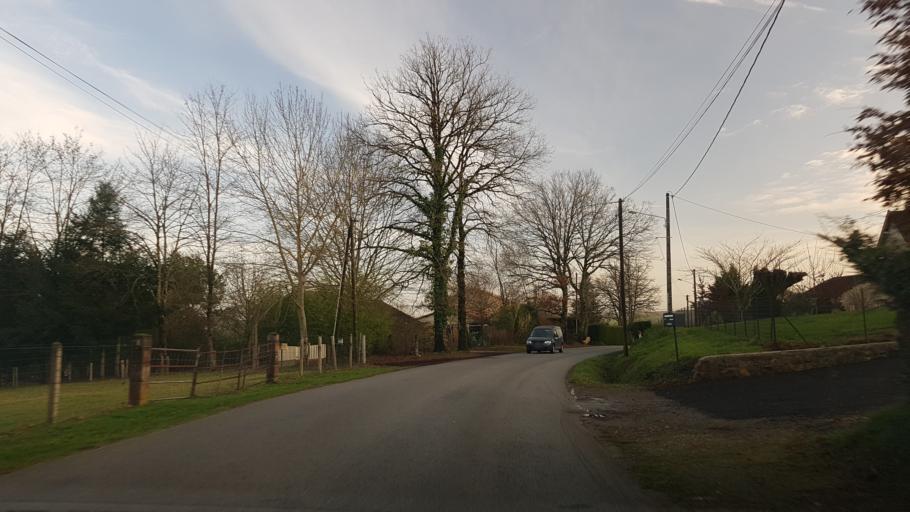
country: FR
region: Limousin
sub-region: Departement de la Haute-Vienne
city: Saint-Junien
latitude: 45.8948
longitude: 0.8755
